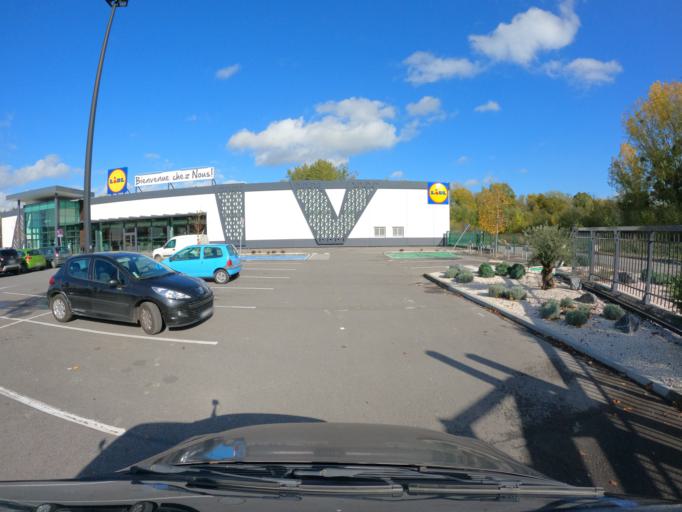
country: FR
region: Ile-de-France
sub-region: Departement de Seine-et-Marne
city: Esbly
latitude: 48.8970
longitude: 2.8162
